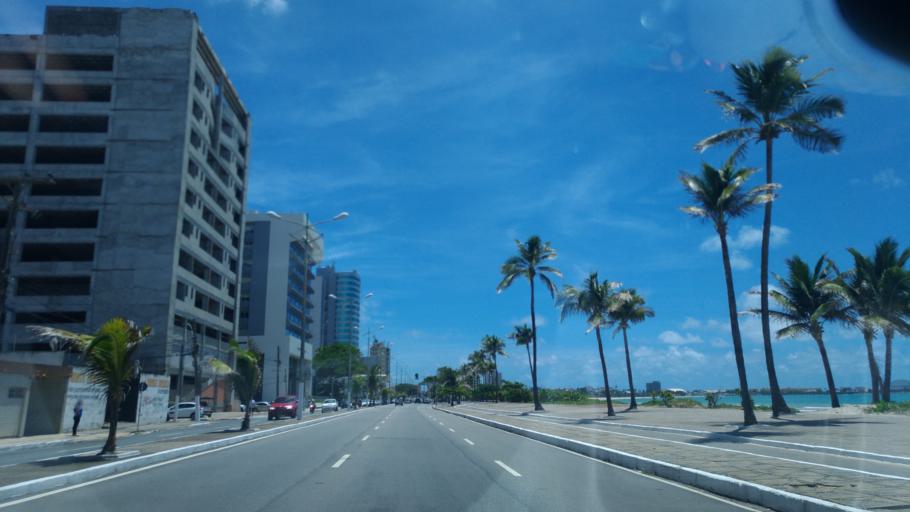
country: BR
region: Alagoas
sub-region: Maceio
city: Maceio
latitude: -9.6703
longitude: -35.7394
